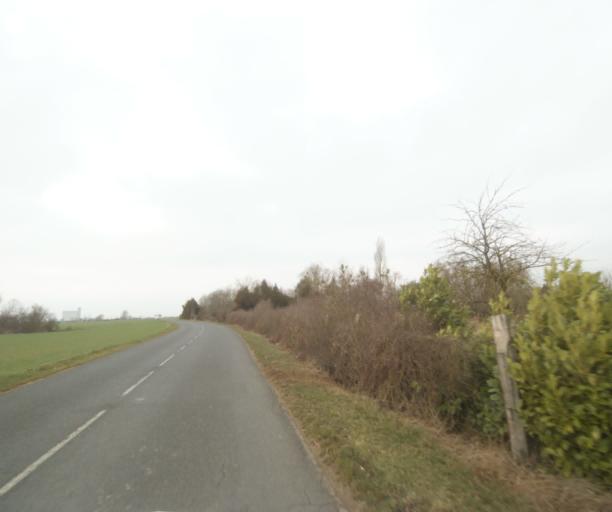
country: FR
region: Champagne-Ardenne
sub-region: Departement de la Haute-Marne
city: Villiers-en-Lieu
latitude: 48.6540
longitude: 4.7862
